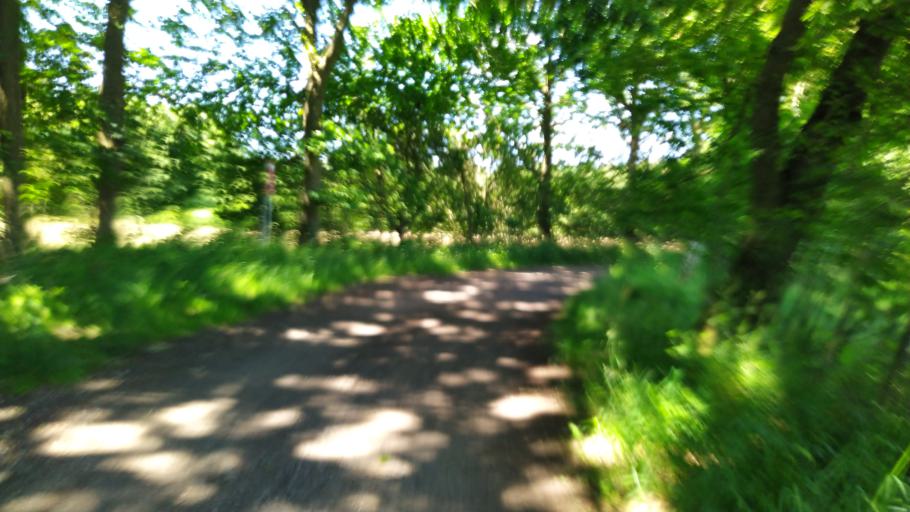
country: DE
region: Lower Saxony
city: Heinbockel
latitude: 53.5507
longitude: 9.2866
